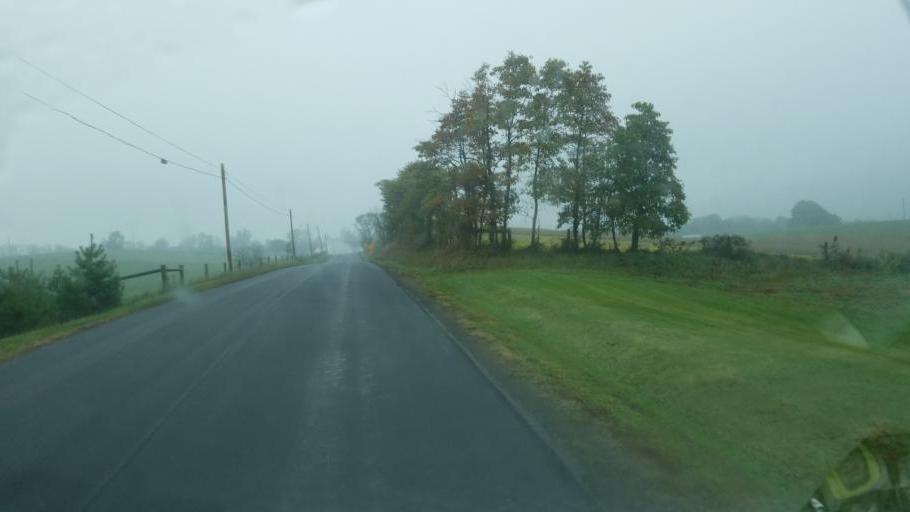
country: US
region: Ohio
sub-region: Tuscarawas County
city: Sugarcreek
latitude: 40.5757
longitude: -81.7352
